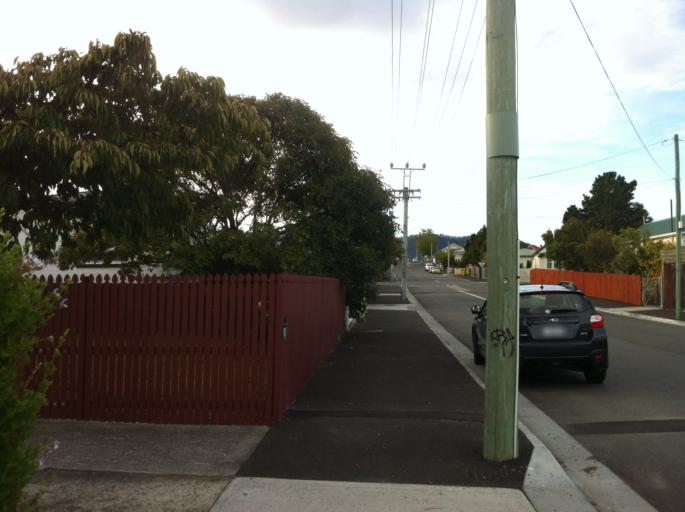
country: AU
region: Tasmania
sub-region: Glenorchy
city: Moonah
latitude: -42.8464
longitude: 147.3044
